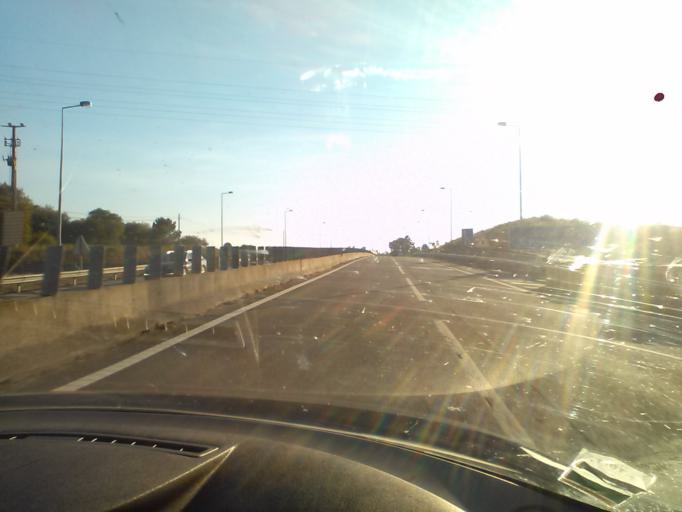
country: PT
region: Porto
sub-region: Vila do Conde
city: Vila do Conde
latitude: 41.3761
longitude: -8.7236
